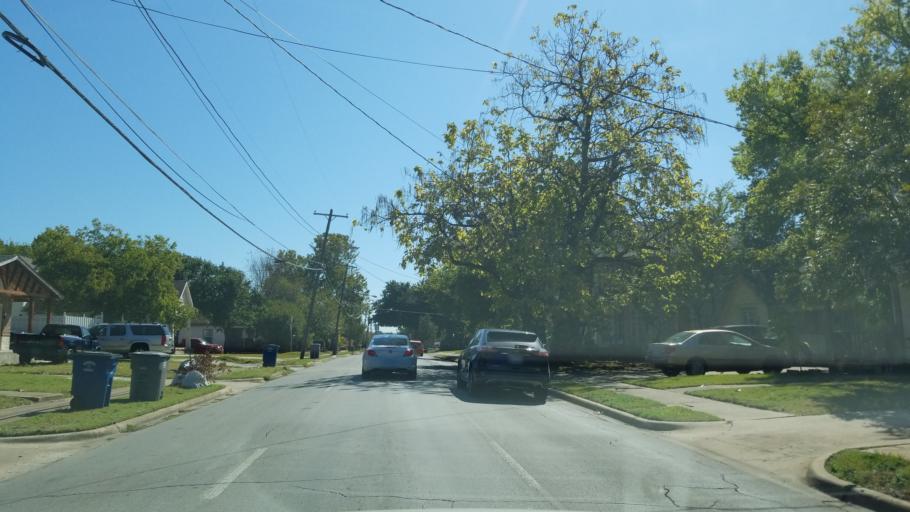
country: US
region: Texas
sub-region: Dallas County
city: Highland Park
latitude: 32.7951
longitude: -96.7505
